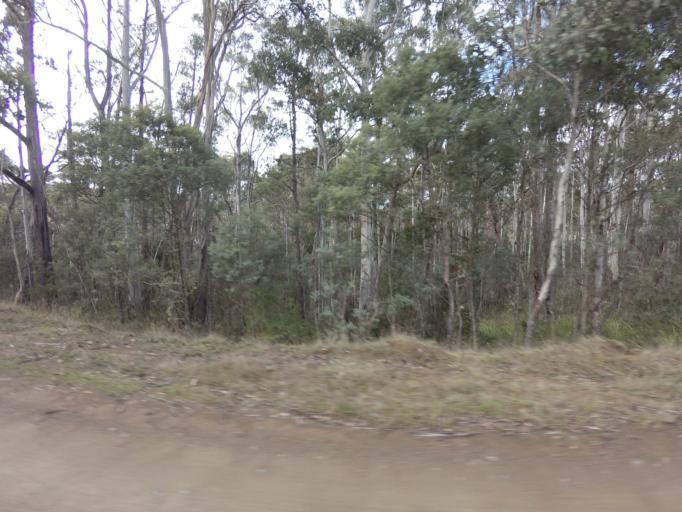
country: AU
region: Tasmania
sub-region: Derwent Valley
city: New Norfolk
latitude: -42.7521
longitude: 146.8754
